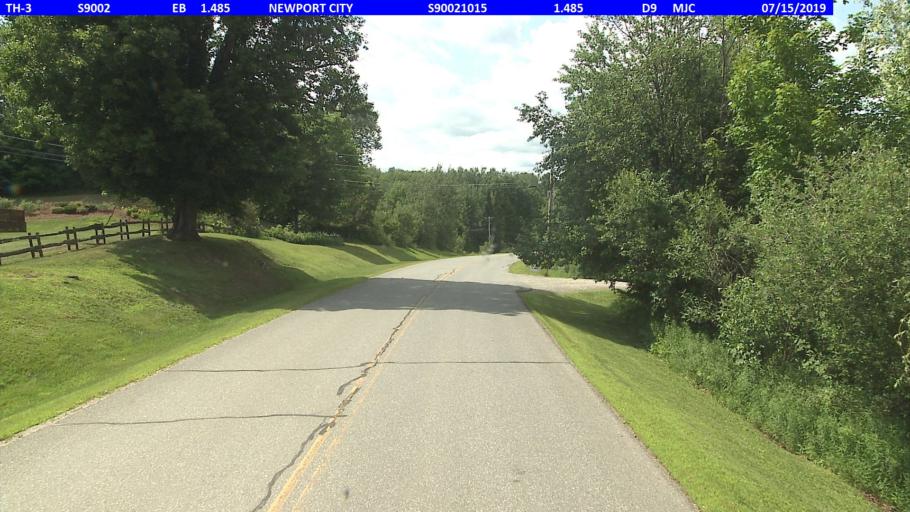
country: US
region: Vermont
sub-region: Orleans County
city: Newport
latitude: 44.9370
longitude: -72.2355
